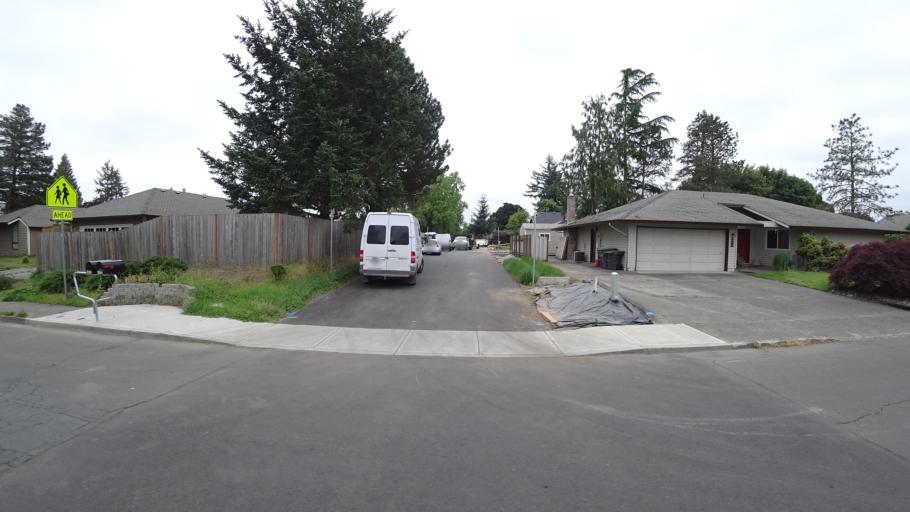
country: US
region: Oregon
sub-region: Washington County
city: Hillsboro
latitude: 45.4983
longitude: -122.9676
